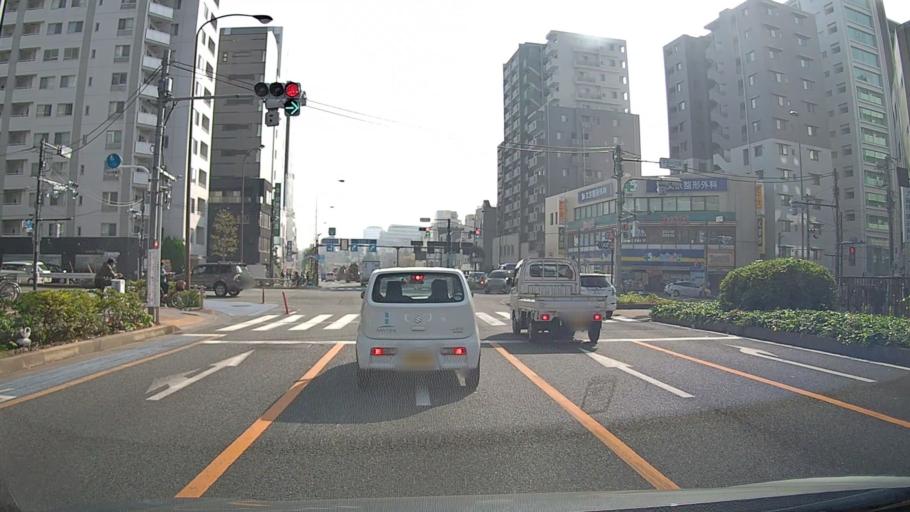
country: JP
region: Tokyo
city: Tokyo
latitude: 35.7290
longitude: 139.7436
